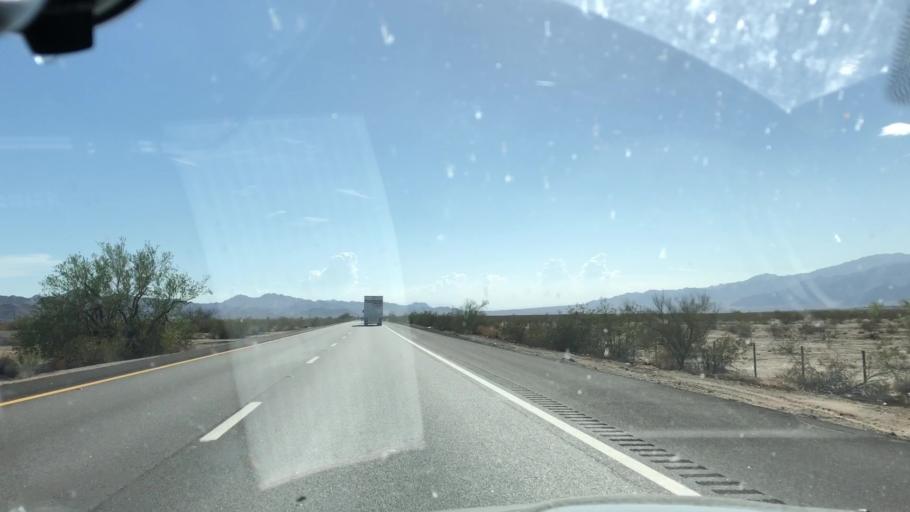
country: US
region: California
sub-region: Imperial County
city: Niland
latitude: 33.6811
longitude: -115.5490
